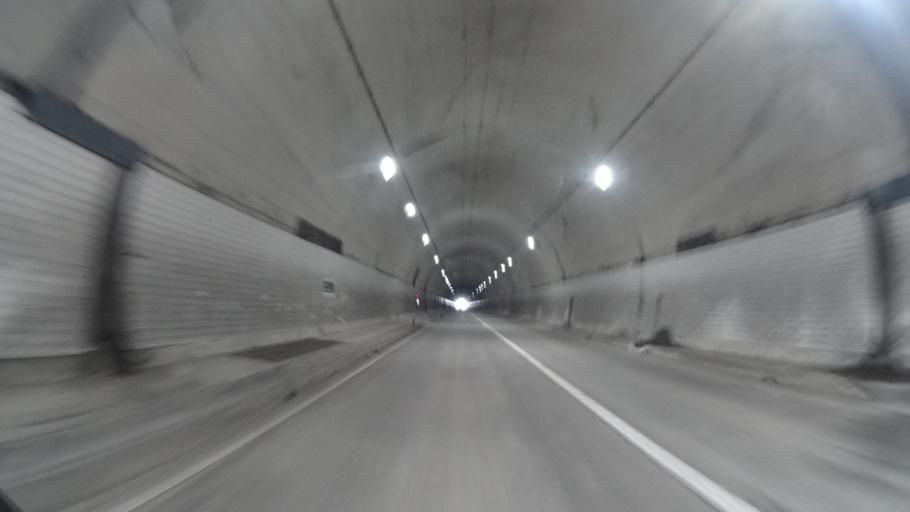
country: JP
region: Ehime
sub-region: Nishiuwa-gun
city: Ikata-cho
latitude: 33.3903
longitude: 132.1354
